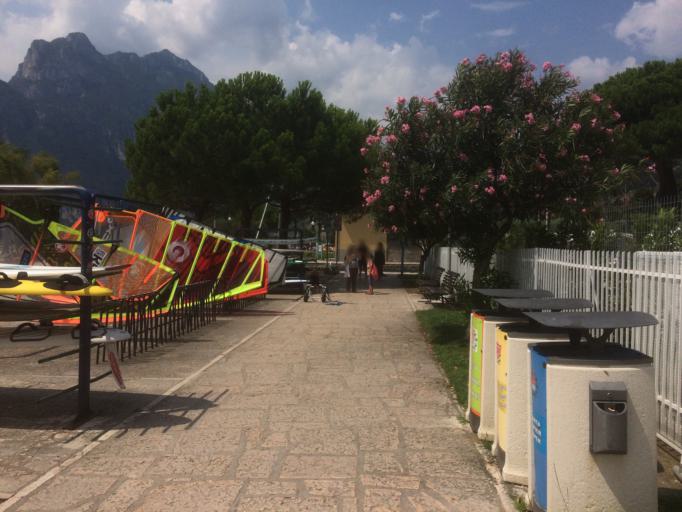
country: IT
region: Trentino-Alto Adige
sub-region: Provincia di Trento
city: Torbole sul Garda
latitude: 45.8705
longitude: 10.8720
